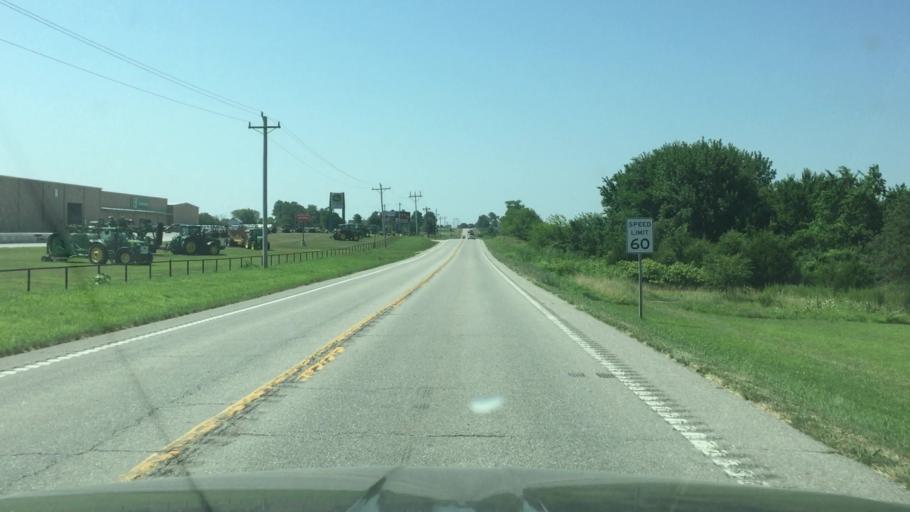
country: US
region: Missouri
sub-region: Moniteau County
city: Tipton
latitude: 38.6222
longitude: -92.7897
